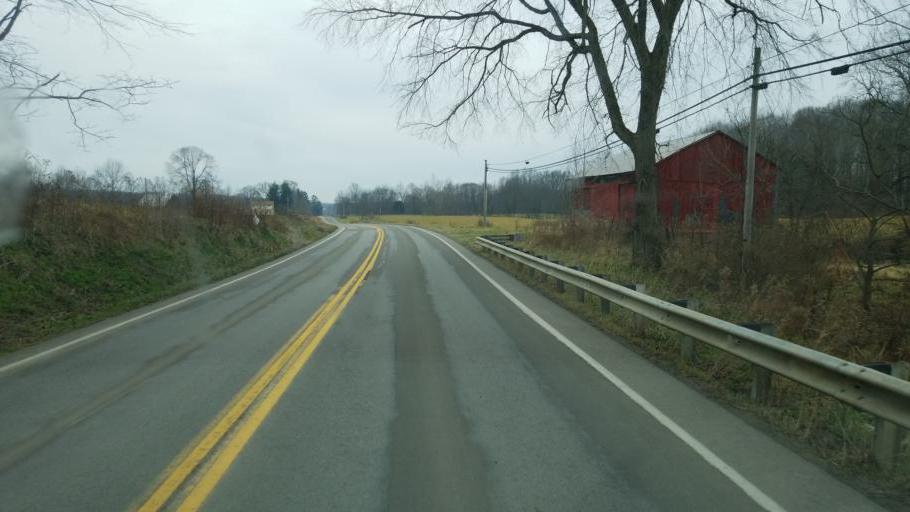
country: US
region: Pennsylvania
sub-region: Crawford County
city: Cochranton
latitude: 41.5259
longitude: -80.1278
